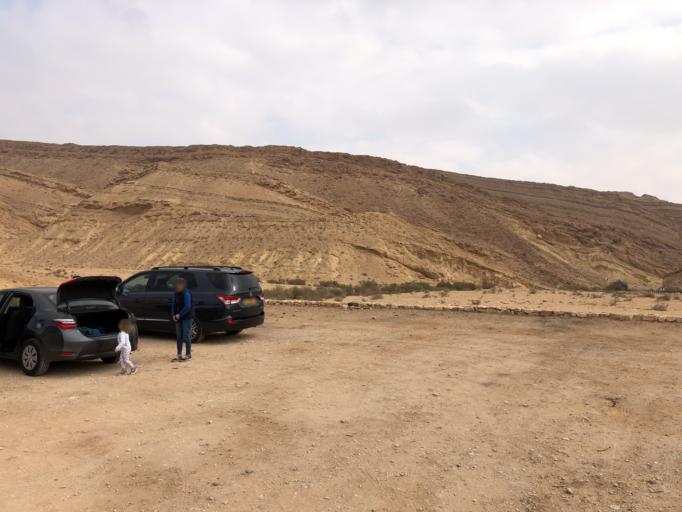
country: IL
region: Southern District
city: Yeroham
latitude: 30.9518
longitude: 35.0261
